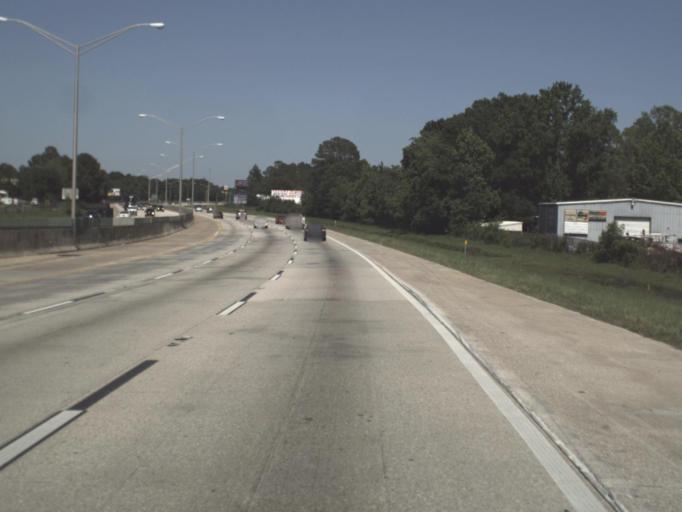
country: US
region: Florida
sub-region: Duval County
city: Jacksonville
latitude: 30.3154
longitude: -81.7420
